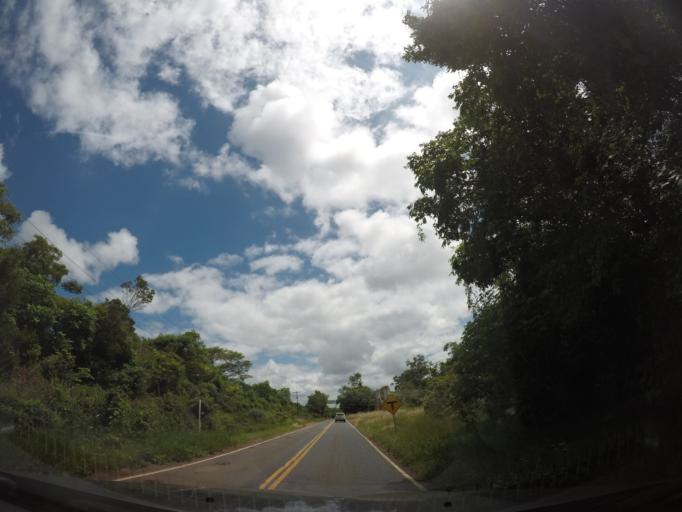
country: BR
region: Bahia
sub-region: Iraquara
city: Iraquara
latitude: -12.4798
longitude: -41.3615
